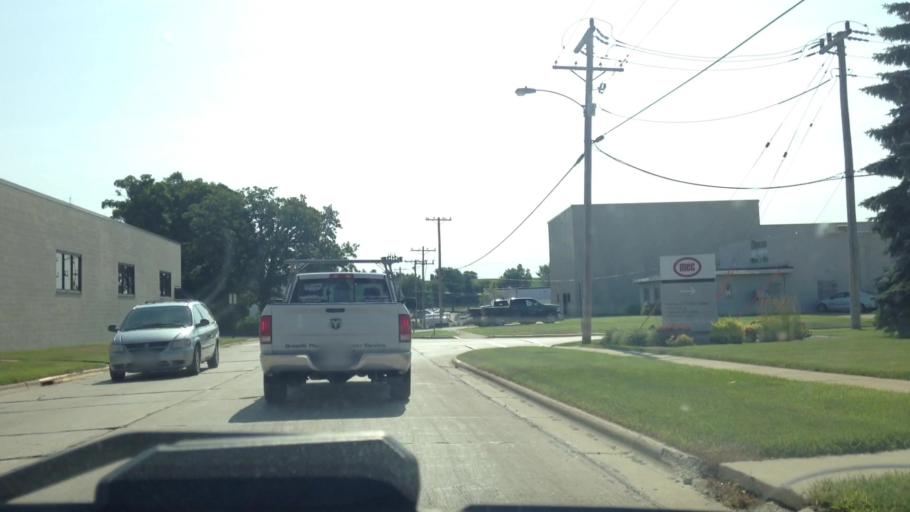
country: US
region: Wisconsin
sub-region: Dodge County
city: Mayville
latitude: 43.4868
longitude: -88.5554
